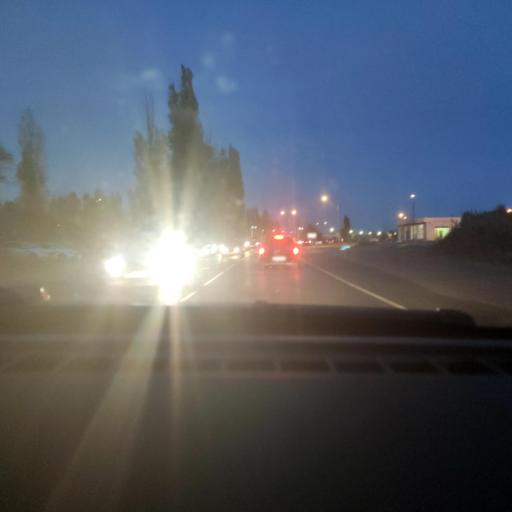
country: RU
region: Voronezj
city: Maslovka
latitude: 51.6221
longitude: 39.2583
